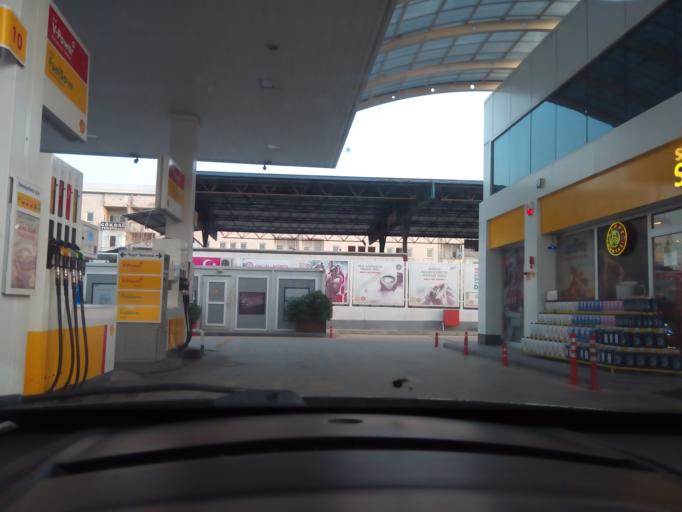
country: TR
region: Bursa
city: Niluefer
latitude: 40.2590
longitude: 28.9525
